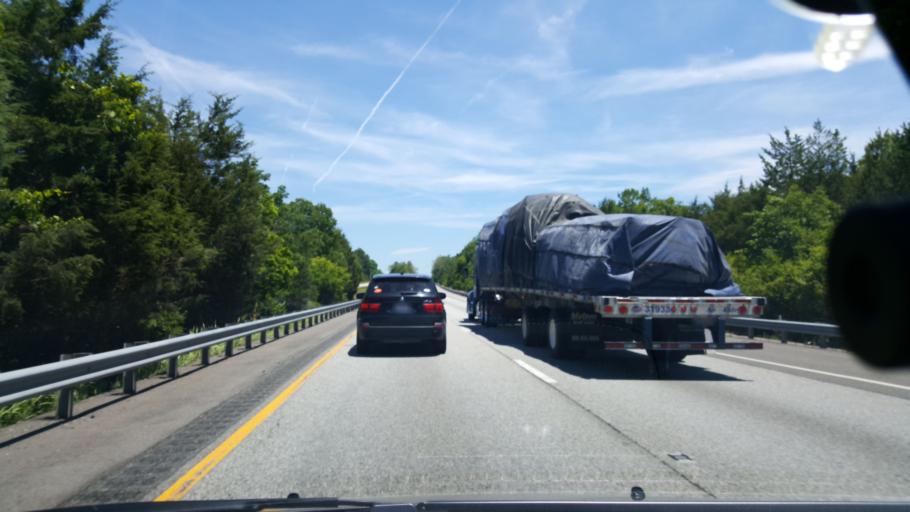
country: US
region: Virginia
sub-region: Botetourt County
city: Fincastle
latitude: 37.4588
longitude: -79.8340
